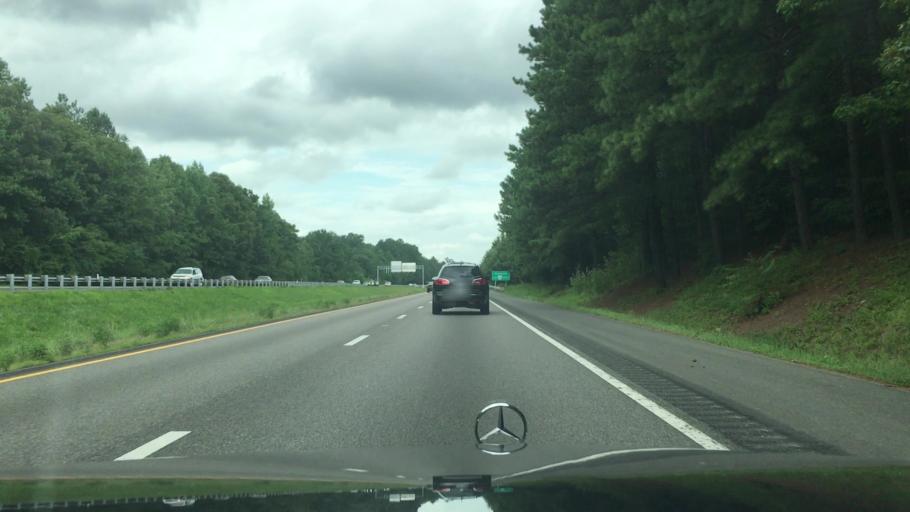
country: US
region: Virginia
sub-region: Chesterfield County
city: Brandermill
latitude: 37.4375
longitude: -77.6348
